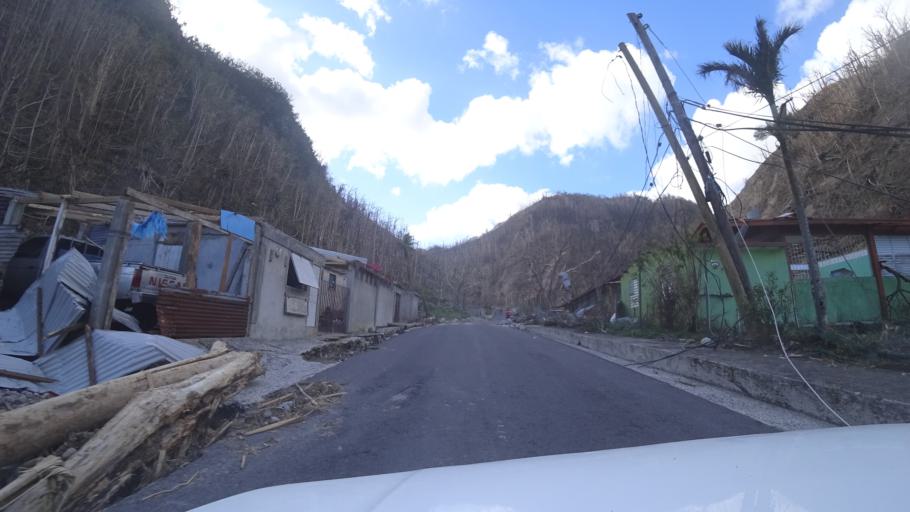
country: DM
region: Saint Patrick
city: Berekua
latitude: 15.2617
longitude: -61.3190
